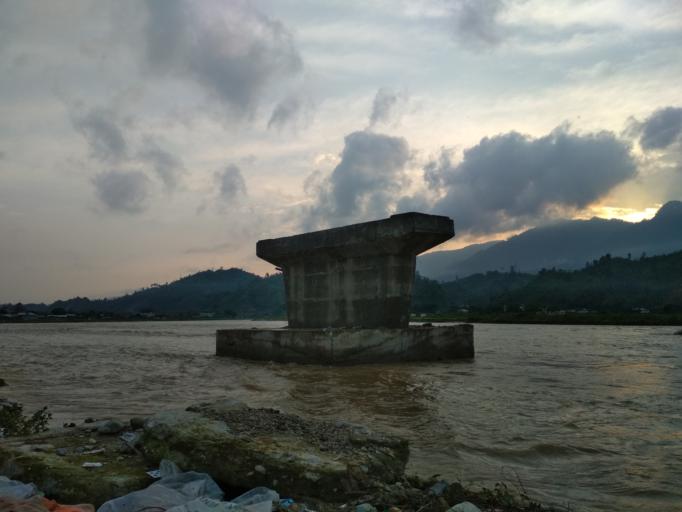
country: IN
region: Arunachal Pradesh
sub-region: Papum Pare
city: Naharlagun
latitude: 27.1197
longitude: 93.7109
